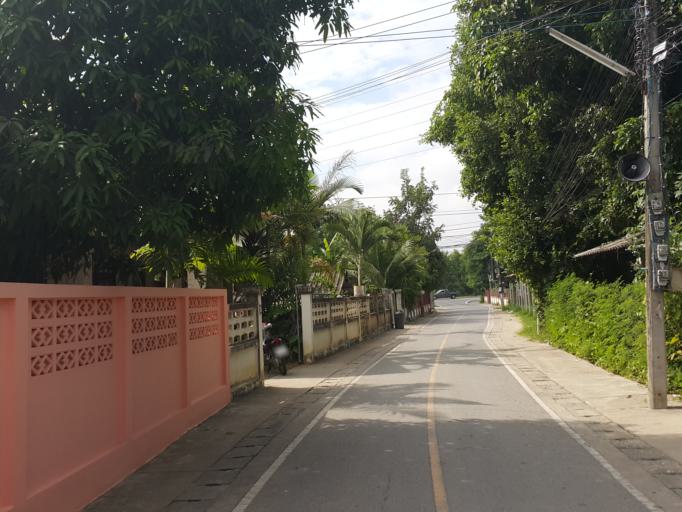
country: TH
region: Chiang Mai
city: San Kamphaeng
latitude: 18.7477
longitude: 99.0709
